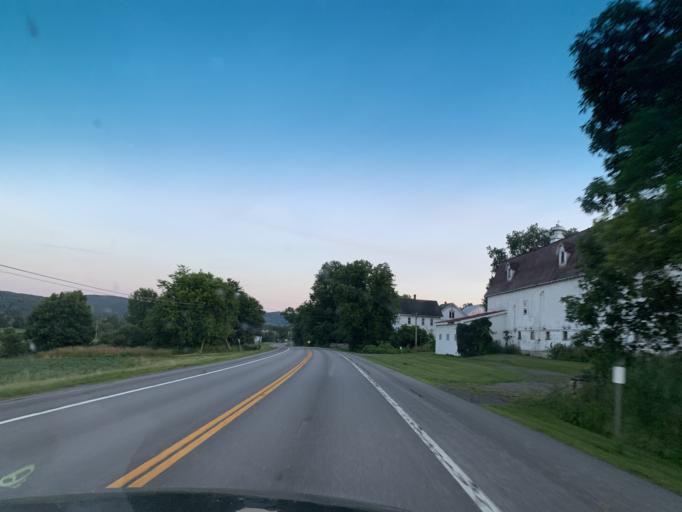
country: US
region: New York
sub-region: Oneida County
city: Waterville
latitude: 42.8179
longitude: -75.2537
